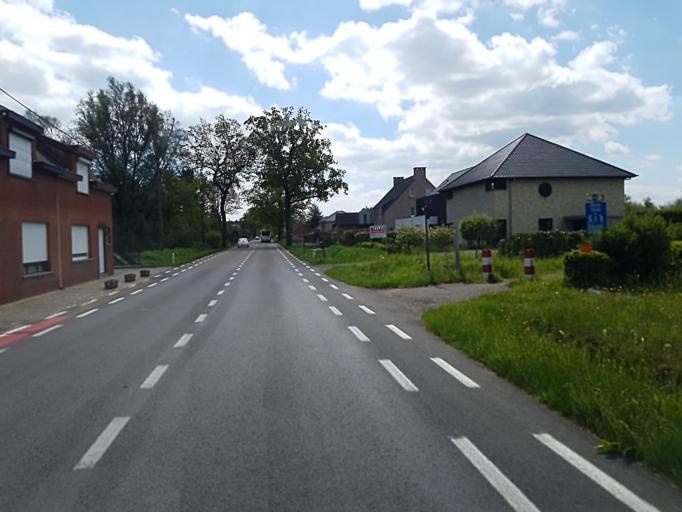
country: BE
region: Flanders
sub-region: Provincie Antwerpen
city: Laakdal
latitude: 51.0585
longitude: 4.9959
